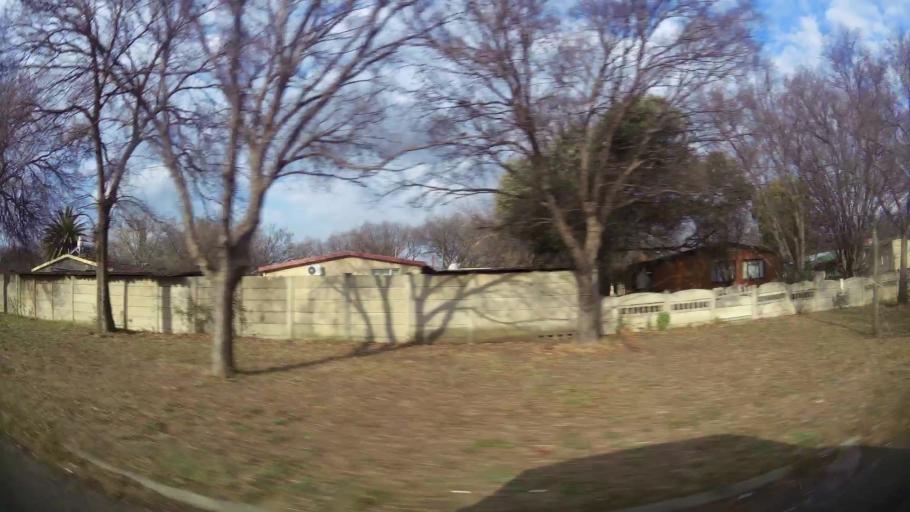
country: ZA
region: Orange Free State
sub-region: Fezile Dabi District Municipality
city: Sasolburg
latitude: -26.8078
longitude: 27.8111
